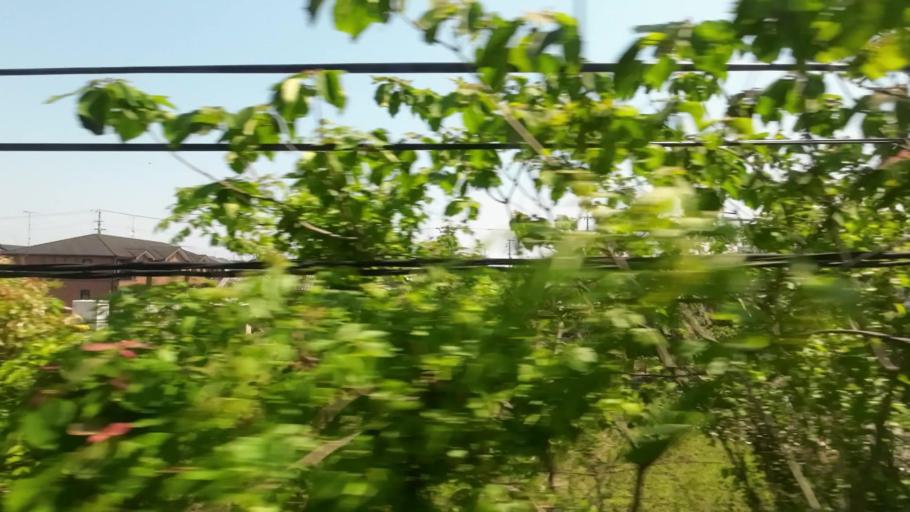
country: JP
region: Ehime
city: Saijo
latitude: 33.9366
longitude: 133.0794
